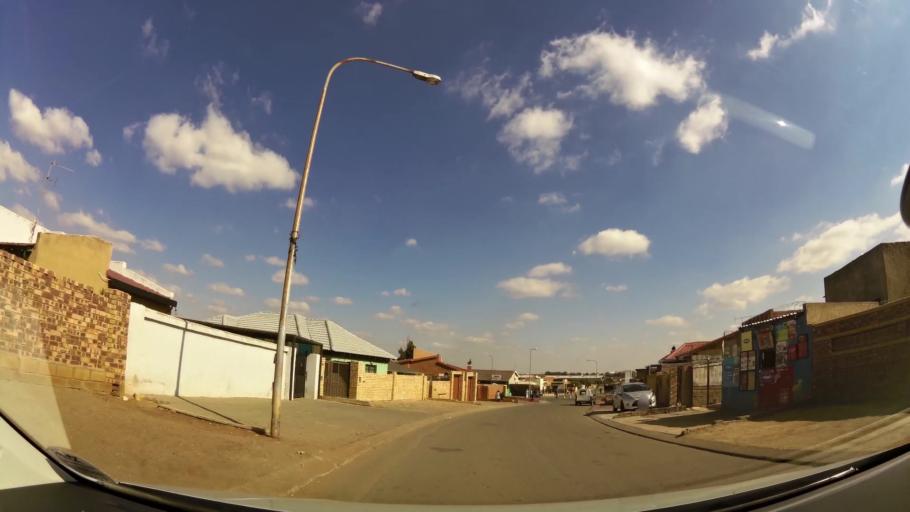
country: ZA
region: Gauteng
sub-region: City of Johannesburg Metropolitan Municipality
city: Roodepoort
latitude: -26.2102
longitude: 27.8808
